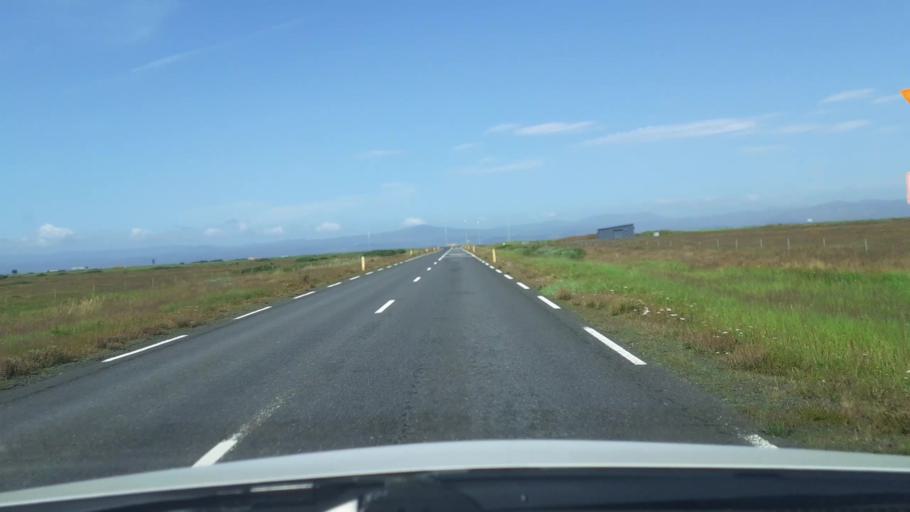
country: IS
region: South
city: Selfoss
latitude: 63.8579
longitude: -21.1066
